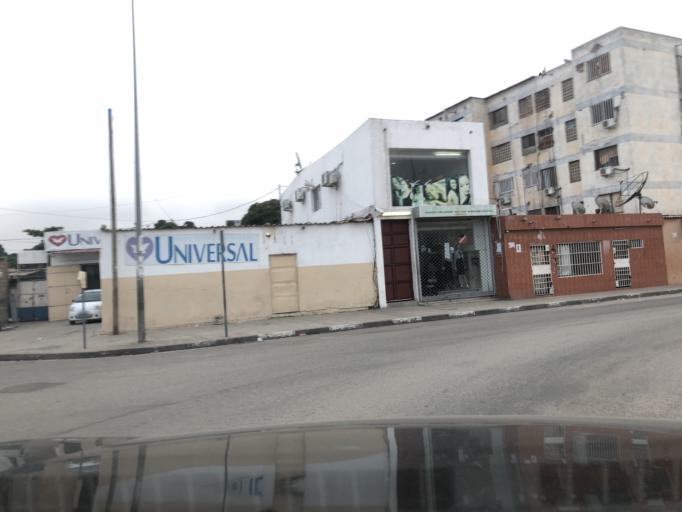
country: AO
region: Luanda
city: Luanda
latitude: -8.8440
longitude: 13.2296
